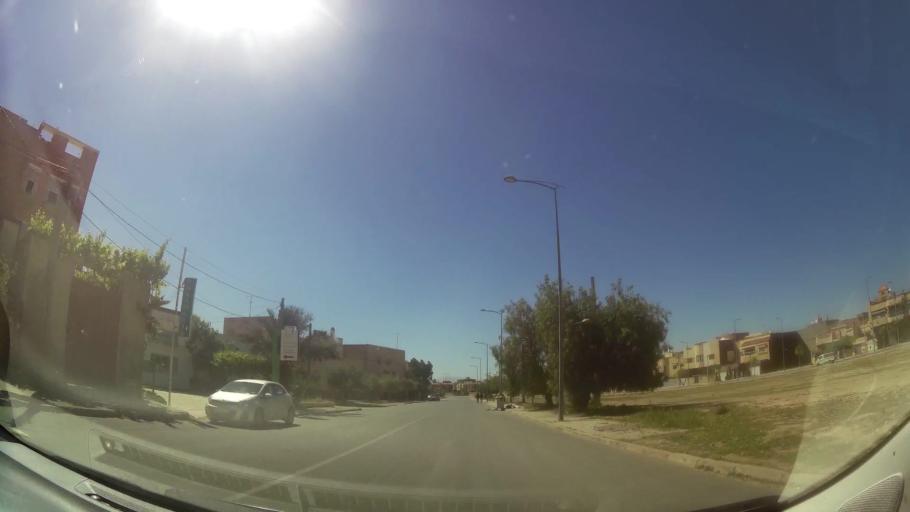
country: MA
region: Oriental
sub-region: Oujda-Angad
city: Oujda
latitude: 34.6668
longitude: -1.8706
